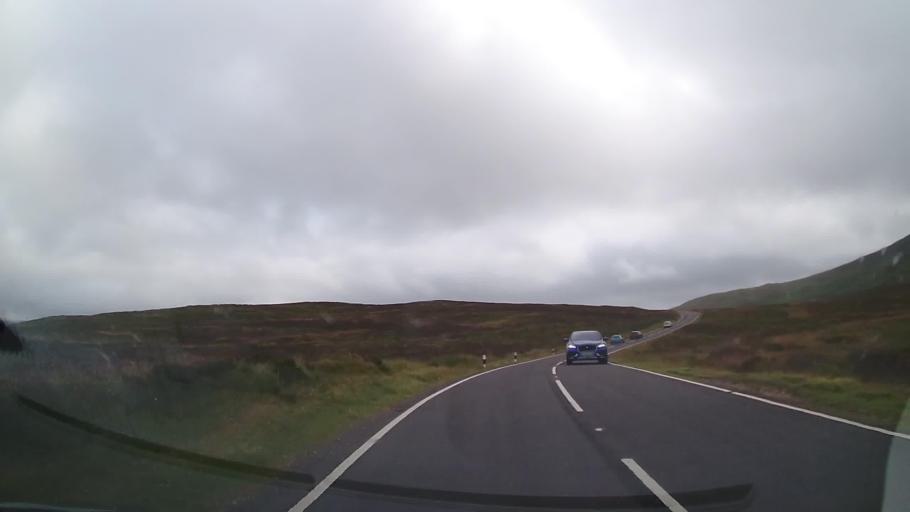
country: GB
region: Wales
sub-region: Denbighshire
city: Llandrillo
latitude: 52.8873
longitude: -3.4842
